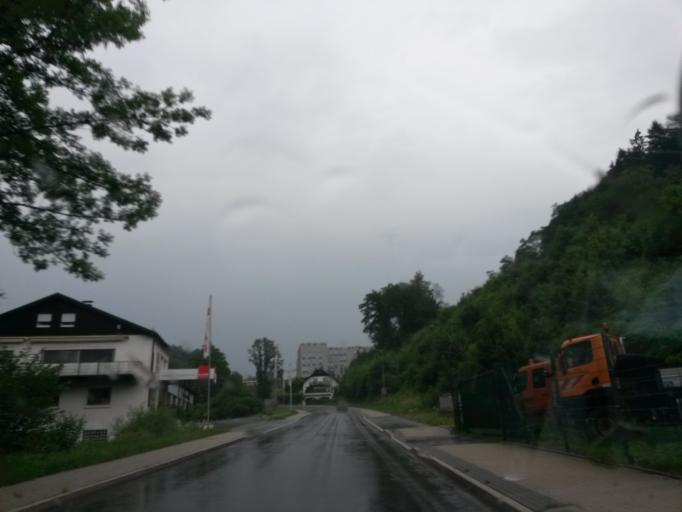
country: DE
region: North Rhine-Westphalia
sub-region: Regierungsbezirk Koln
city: Gummersbach
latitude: 51.0181
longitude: 7.5621
